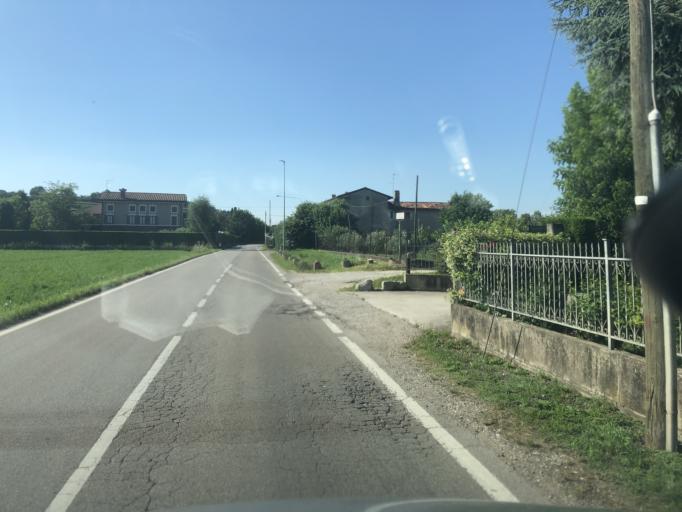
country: IT
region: Veneto
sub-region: Provincia di Verona
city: Villafranca di Verona
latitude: 45.3773
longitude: 10.8271
